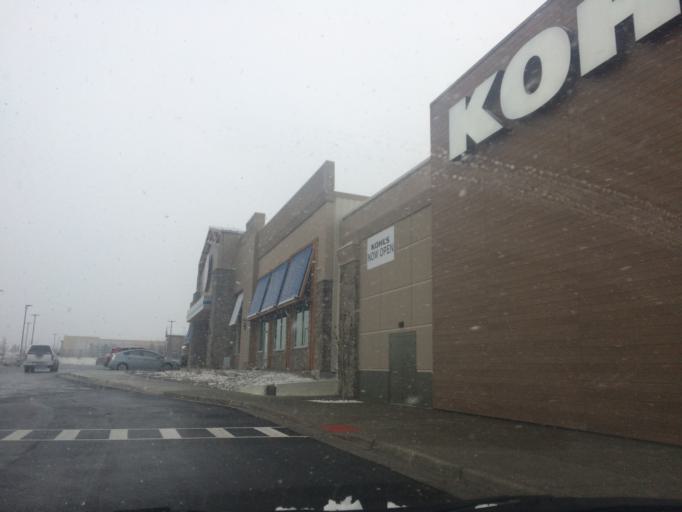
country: US
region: Colorado
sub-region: Boulder County
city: Lafayette
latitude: 40.0095
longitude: -105.1048
